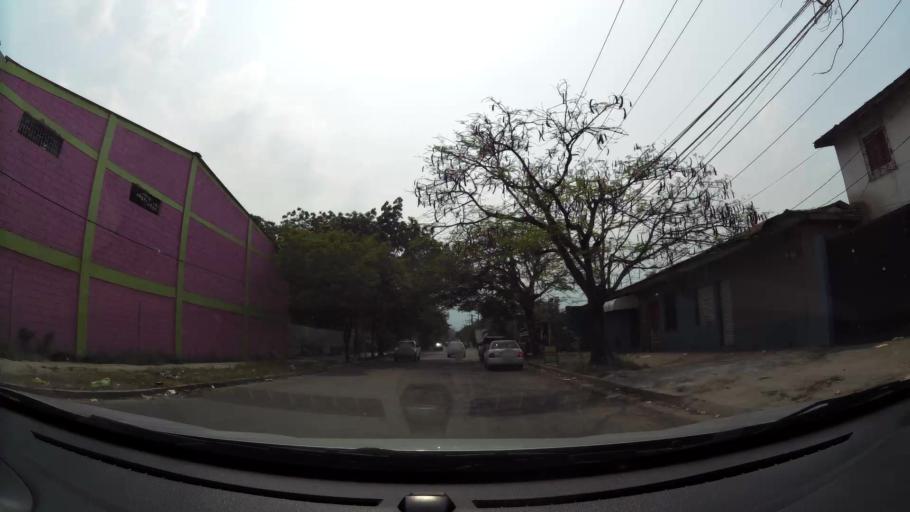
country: HN
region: Cortes
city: San Pedro Sula
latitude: 15.4872
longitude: -88.0211
